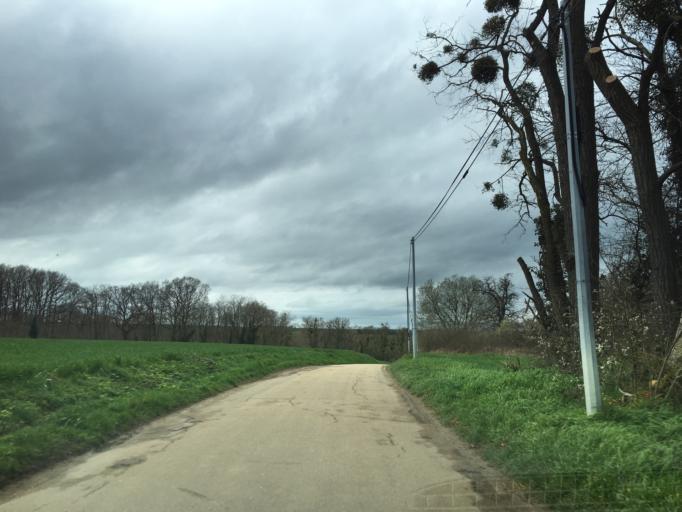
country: FR
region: Bourgogne
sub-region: Departement de l'Yonne
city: Charbuy
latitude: 47.8385
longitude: 3.4485
